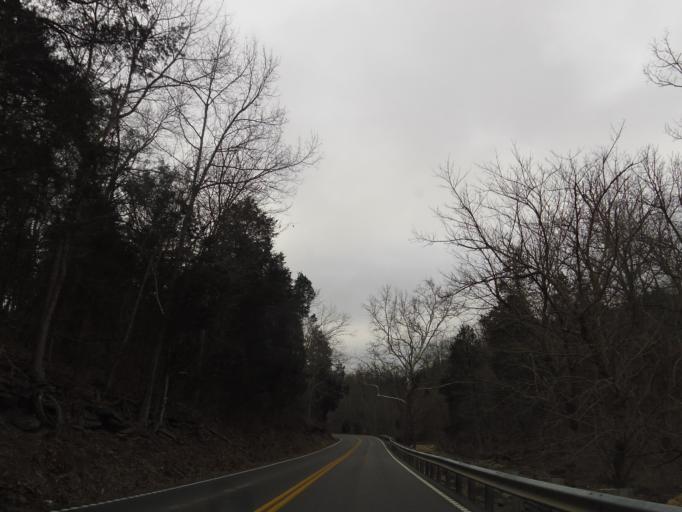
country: US
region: Kentucky
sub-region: Franklin County
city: Frankfort
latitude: 38.2530
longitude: -84.9320
